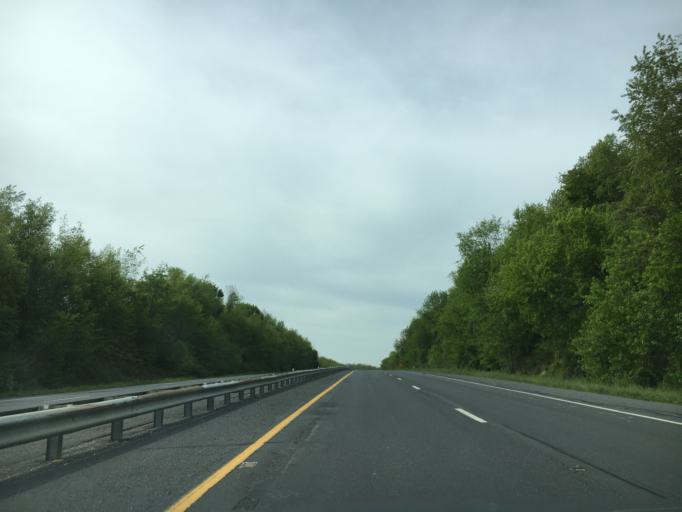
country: US
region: Pennsylvania
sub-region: Lehigh County
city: Cementon
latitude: 40.7034
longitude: -75.5211
